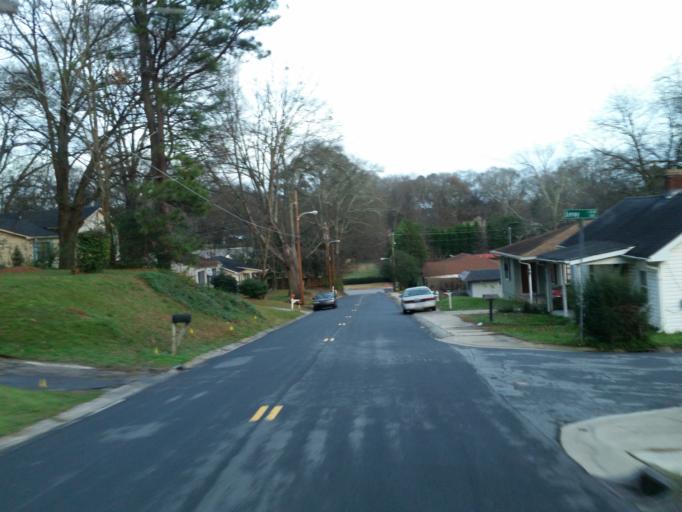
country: US
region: Georgia
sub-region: Cobb County
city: Marietta
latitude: 33.9542
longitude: -84.5366
